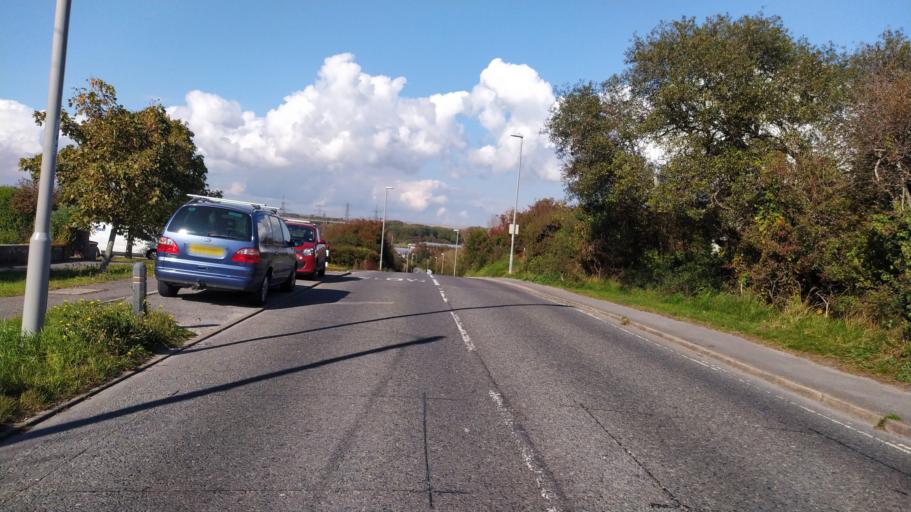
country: GB
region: England
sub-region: Dorset
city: Weymouth
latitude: 50.6153
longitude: -2.4822
